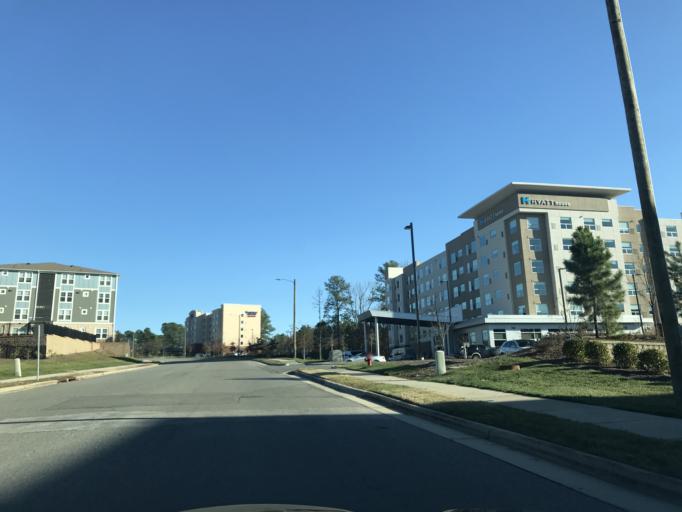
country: US
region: North Carolina
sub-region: Wake County
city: Morrisville
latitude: 35.8962
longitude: -78.8073
